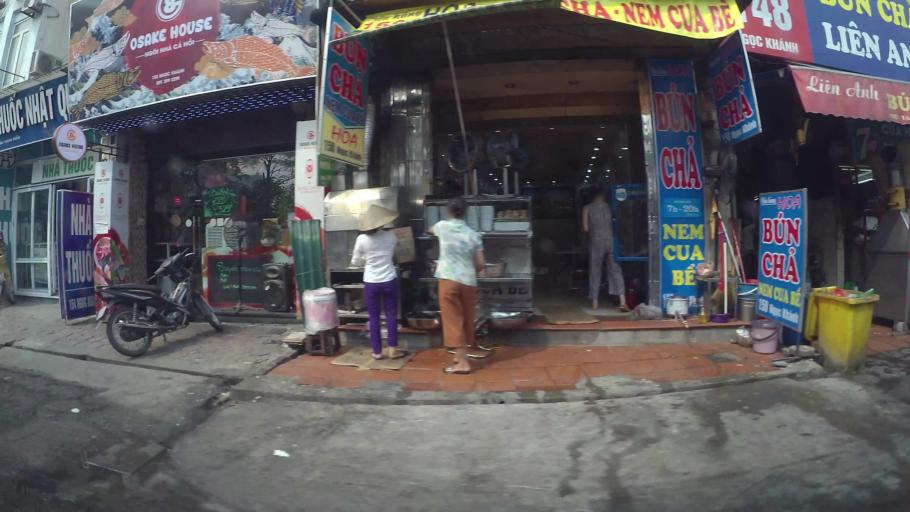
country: VN
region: Ha Noi
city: Dong Da
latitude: 21.0257
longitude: 105.8183
